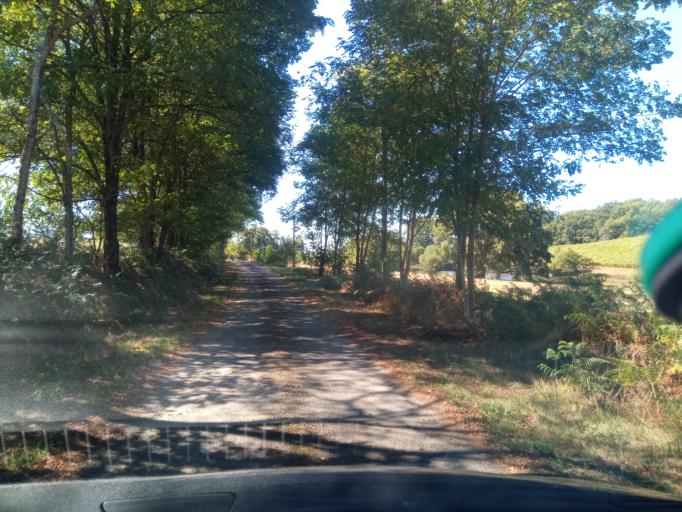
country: FR
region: Limousin
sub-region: Departement de la Haute-Vienne
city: Nantiat
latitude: 46.0647
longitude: 1.2051
